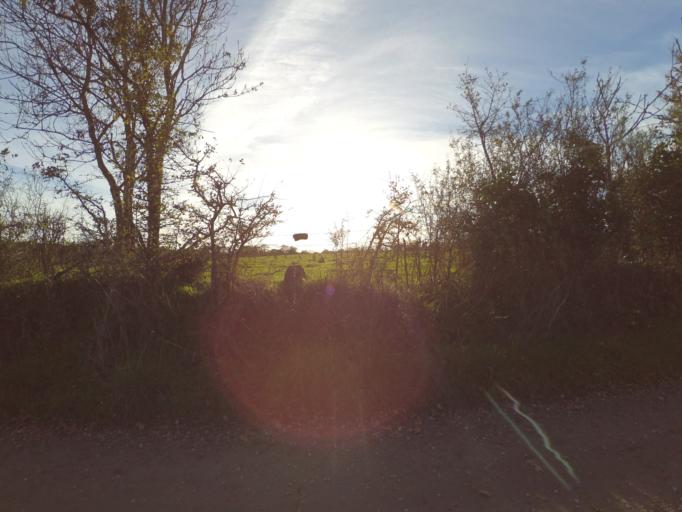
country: FR
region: Pays de la Loire
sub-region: Departement de la Vendee
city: Saint-Hilaire-de-Loulay
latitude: 47.0140
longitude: -1.3496
